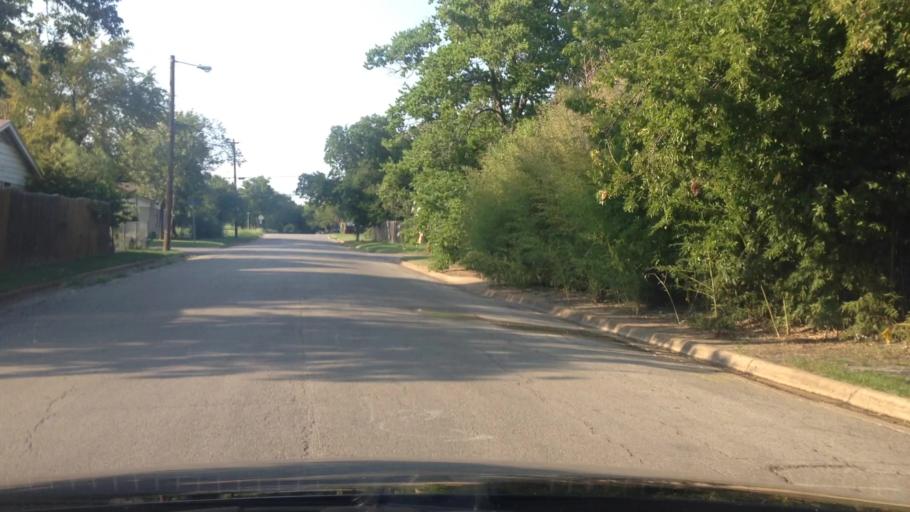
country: US
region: Texas
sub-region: Tarrant County
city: Everman
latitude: 32.6297
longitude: -97.2917
